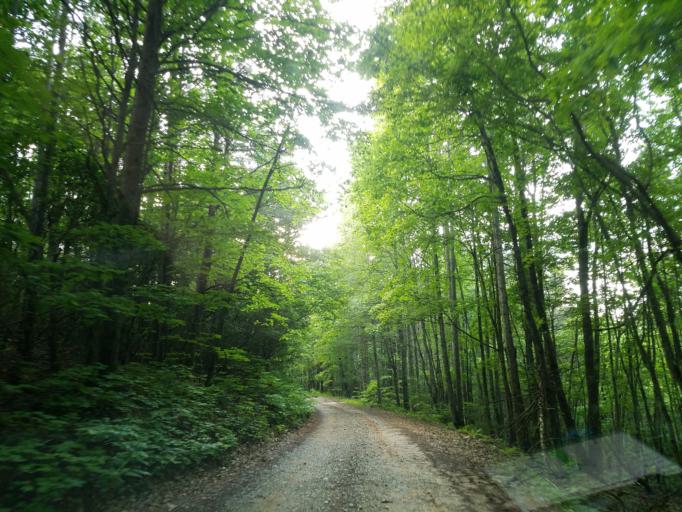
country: US
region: Georgia
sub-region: Dawson County
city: Dawsonville
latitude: 34.5760
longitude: -84.1435
